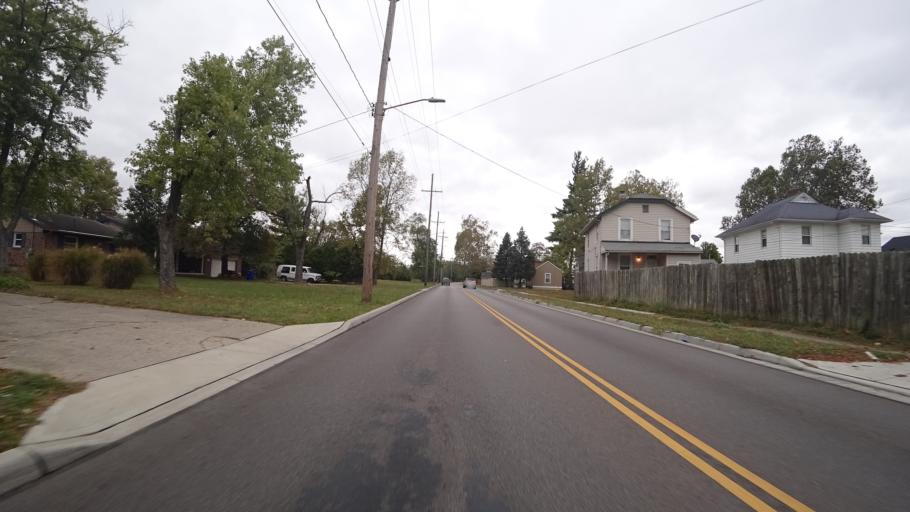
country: US
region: Ohio
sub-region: Butler County
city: Fairfield
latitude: 39.3658
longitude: -84.5631
